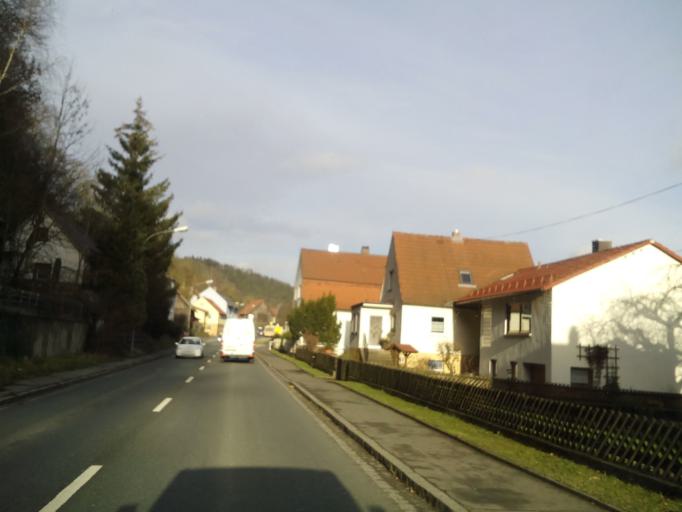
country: DE
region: Bavaria
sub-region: Upper Franconia
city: Untersteinach
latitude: 50.1168
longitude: 11.5025
